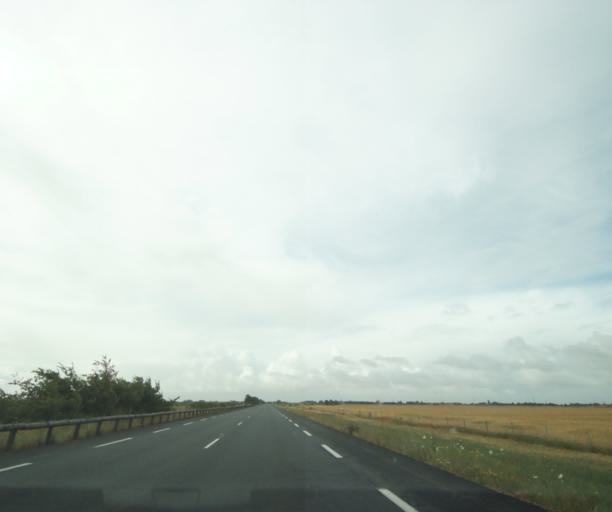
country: FR
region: Pays de la Loire
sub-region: Departement de la Vendee
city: Champagne-les-Marais
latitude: 46.3937
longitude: -1.0947
